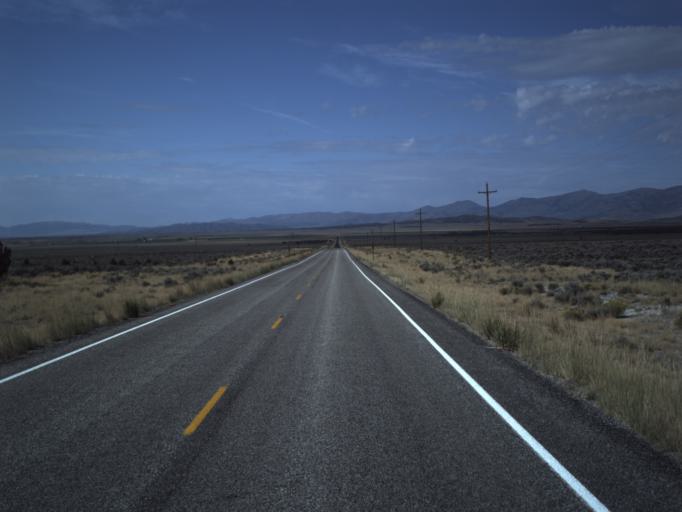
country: US
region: Idaho
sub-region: Cassia County
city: Burley
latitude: 41.8002
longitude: -113.4582
